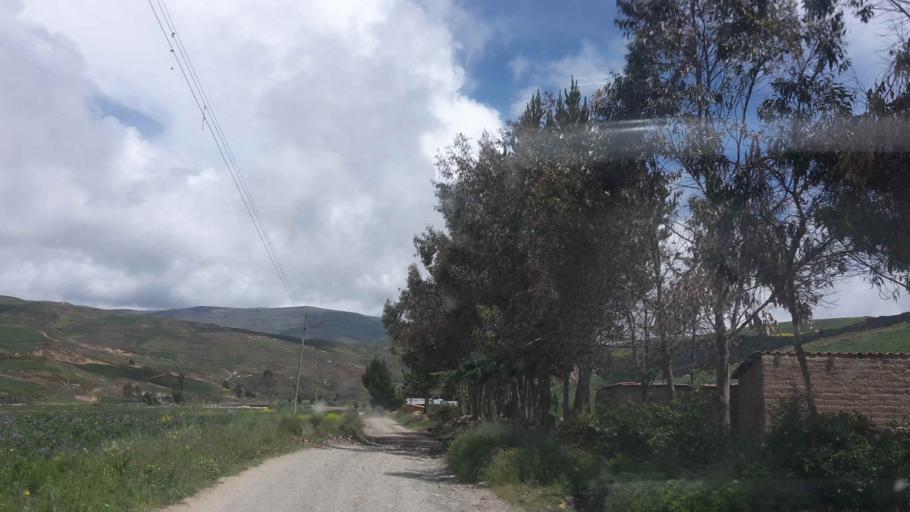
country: BO
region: Cochabamba
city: Cochabamba
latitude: -17.2150
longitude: -66.0844
